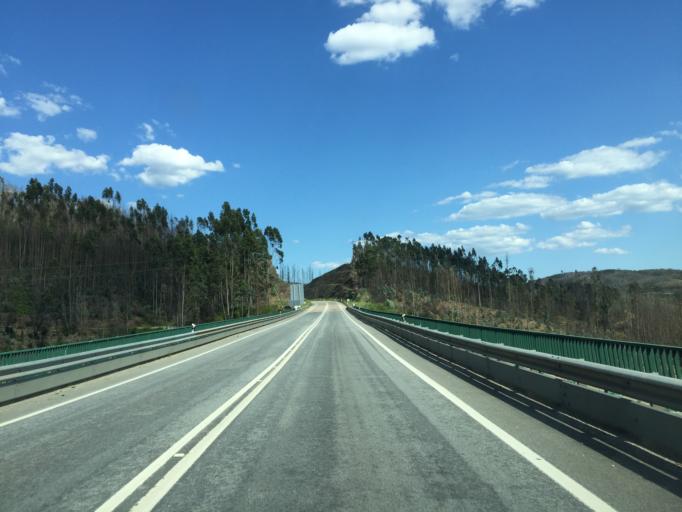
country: PT
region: Leiria
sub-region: Figueiro Dos Vinhos
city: Figueiro dos Vinhos
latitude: 39.9266
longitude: -8.3235
